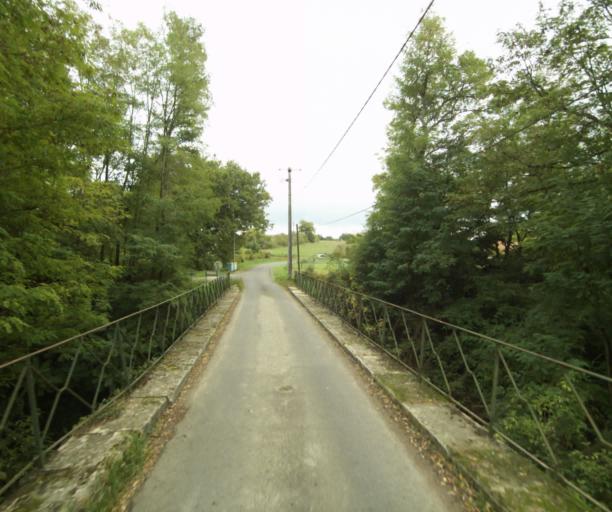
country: FR
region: Midi-Pyrenees
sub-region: Departement du Gers
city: Eauze
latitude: 43.8857
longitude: 0.1073
